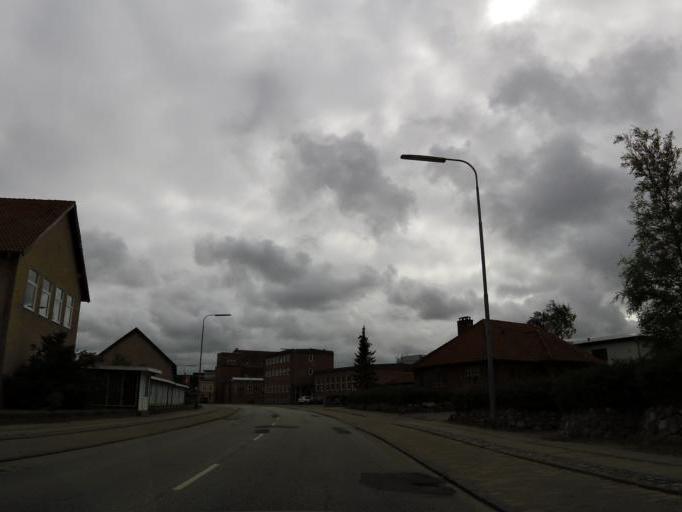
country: DK
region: South Denmark
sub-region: Tonder Kommune
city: Tonder
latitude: 54.9366
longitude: 8.8634
